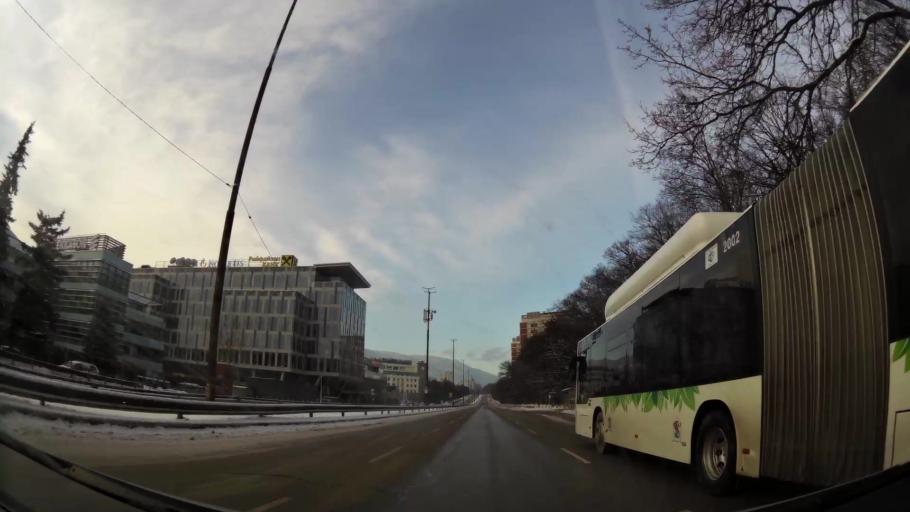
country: BG
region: Sofia-Capital
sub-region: Stolichna Obshtina
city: Sofia
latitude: 42.6677
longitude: 23.3262
